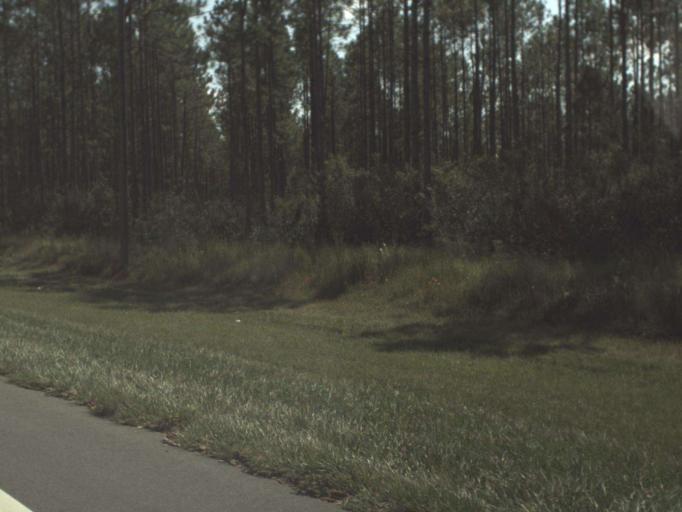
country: US
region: Florida
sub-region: Gulf County
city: Wewahitchka
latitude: 30.1356
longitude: -85.3692
